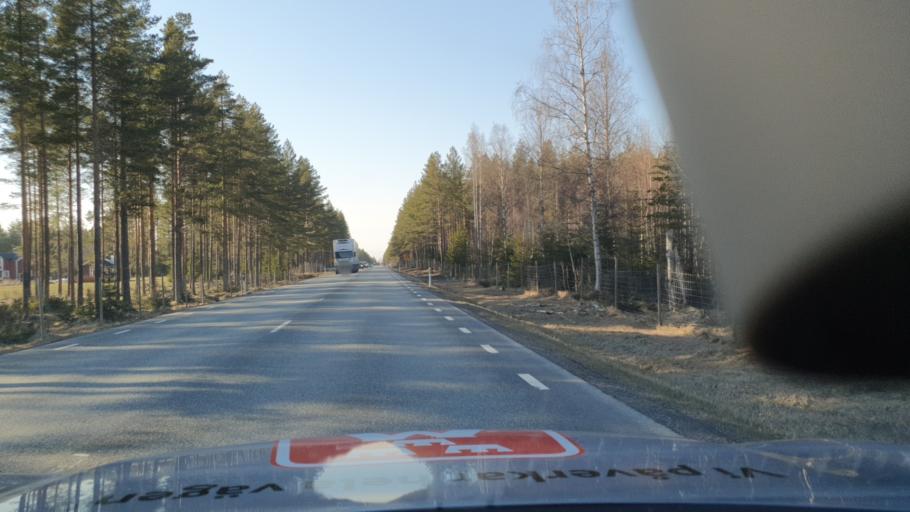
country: SE
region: Vaesterbotten
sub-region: Skelleftea Kommun
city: Burea
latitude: 64.5581
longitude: 21.2384
